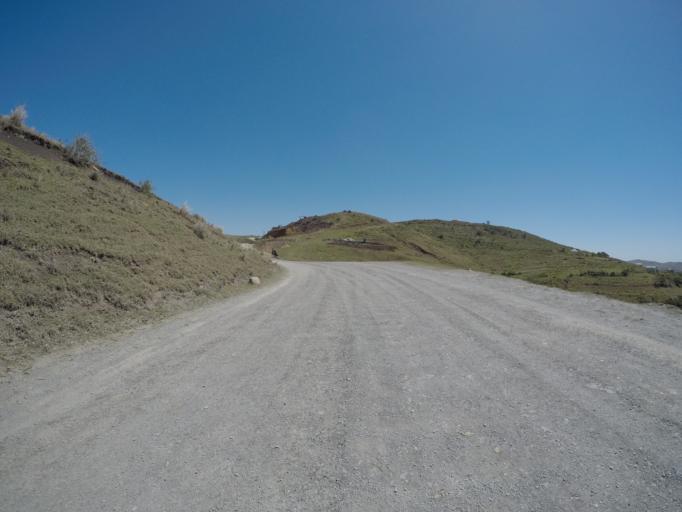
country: ZA
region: Eastern Cape
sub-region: OR Tambo District Municipality
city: Libode
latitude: -32.0134
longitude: 29.0764
